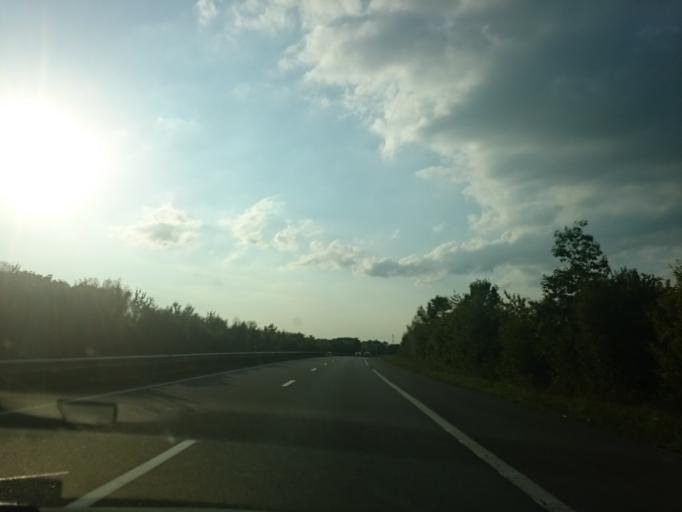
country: FR
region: Pays de la Loire
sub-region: Departement de la Loire-Atlantique
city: La Chapelle-Launay
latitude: 47.3783
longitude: -1.9565
